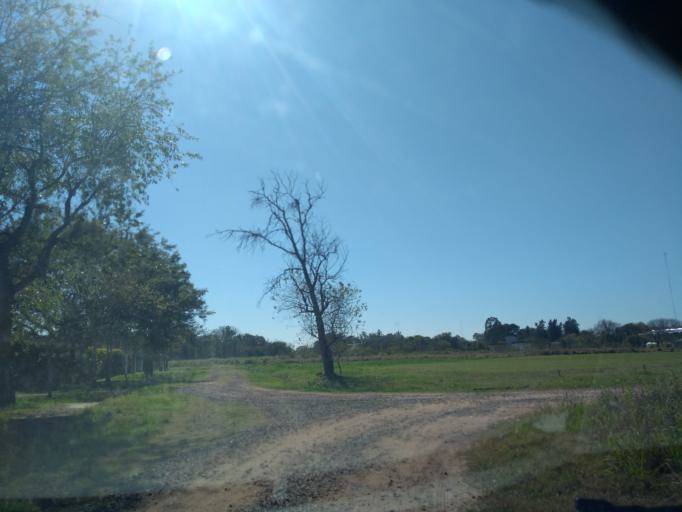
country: AR
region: Chaco
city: Resistencia
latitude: -27.4229
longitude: -58.9443
